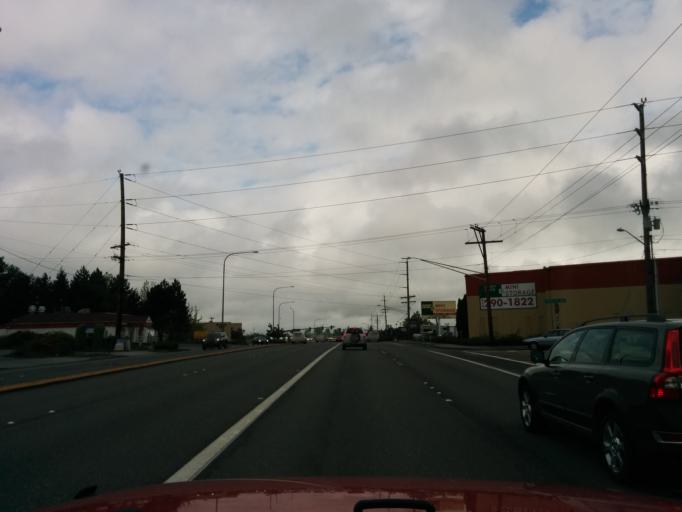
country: US
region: Washington
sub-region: Snohomish County
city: Martha Lake
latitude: 47.8880
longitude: -122.2837
